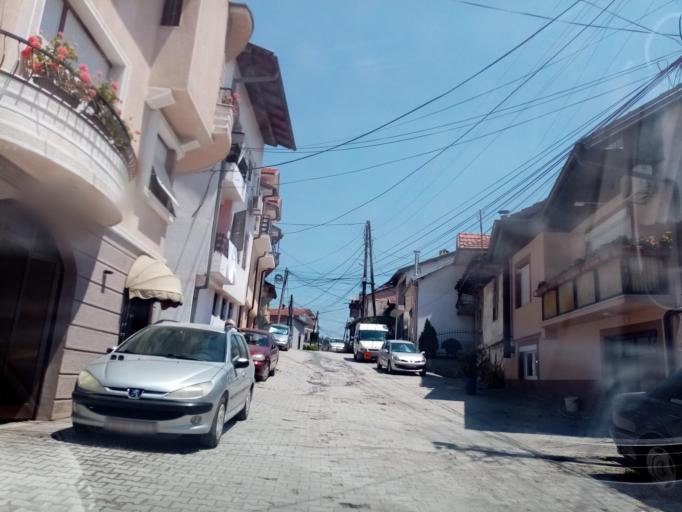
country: MK
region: Tetovo
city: Tetovo
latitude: 42.0162
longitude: 20.9709
